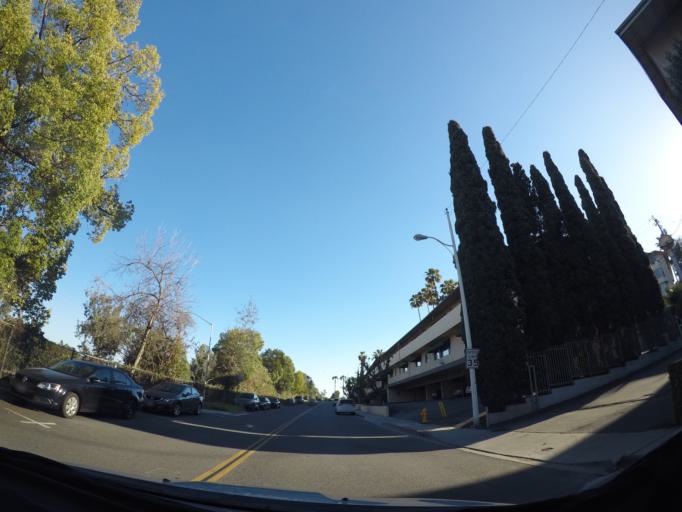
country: US
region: California
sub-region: Los Angeles County
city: South Pasadena
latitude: 34.1232
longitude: -118.1463
